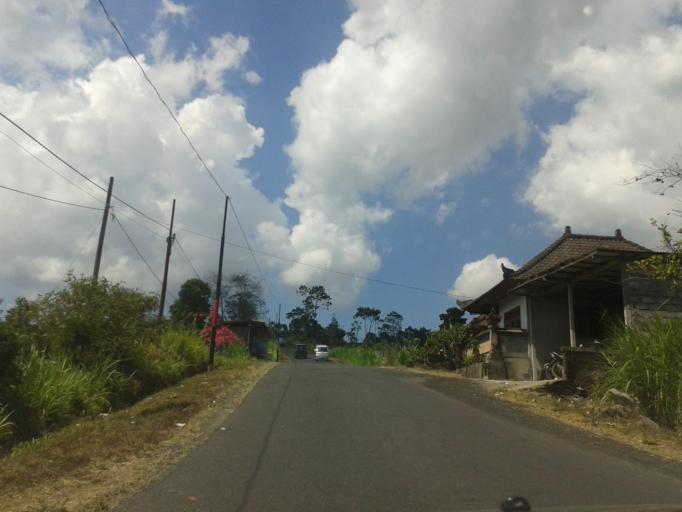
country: ID
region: Bali
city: Banjar Kedisan
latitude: -8.2833
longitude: 115.3500
